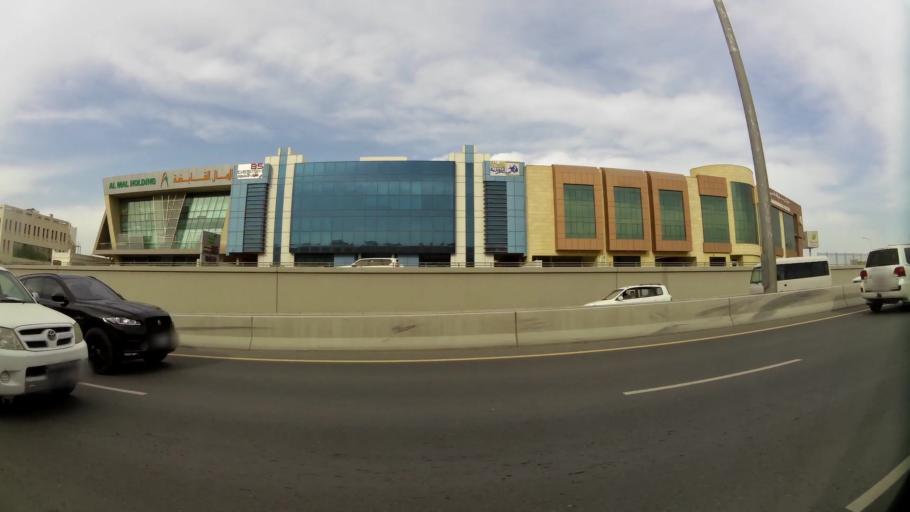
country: QA
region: Baladiyat ad Dawhah
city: Doha
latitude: 25.2731
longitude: 51.4906
